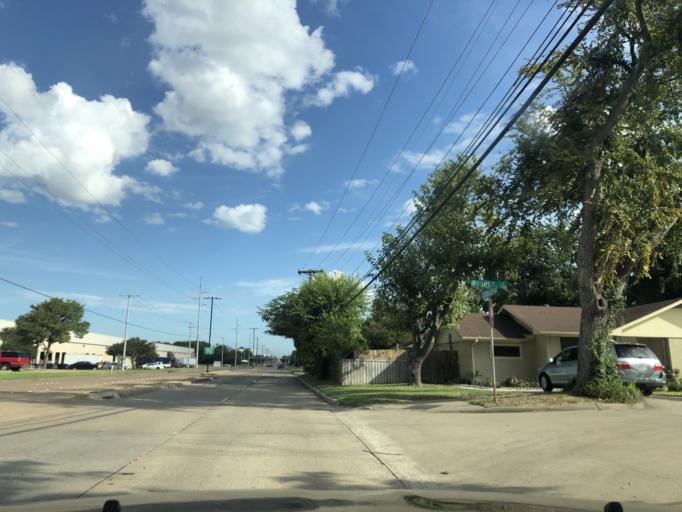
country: US
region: Texas
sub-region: Dallas County
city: Garland
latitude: 32.8832
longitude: -96.6655
